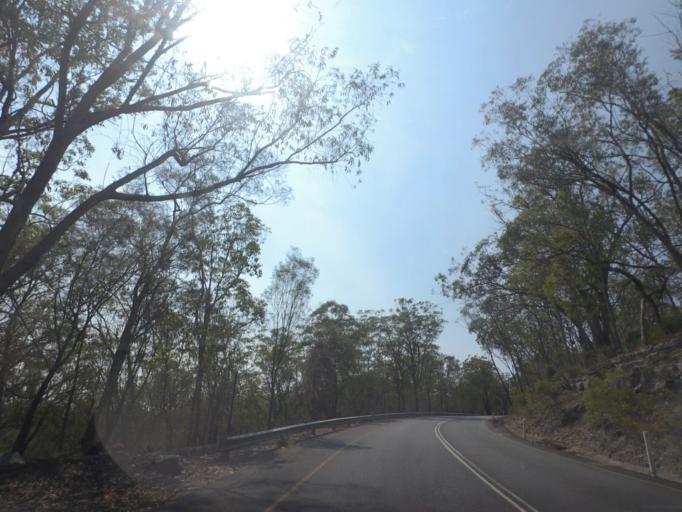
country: AU
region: Queensland
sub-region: Brisbane
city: Nathan
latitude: -27.5554
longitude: 153.0514
